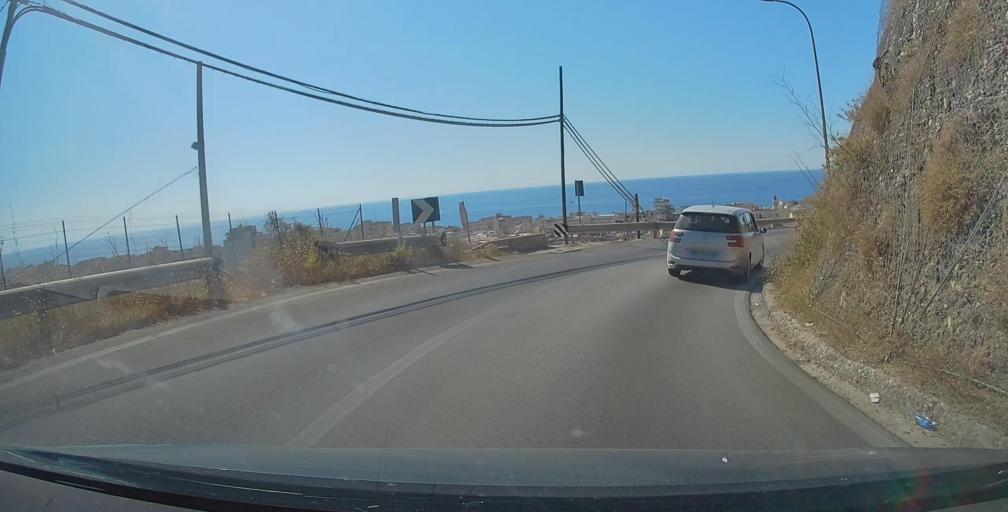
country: IT
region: Sicily
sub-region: Messina
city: Capo d'Orlando
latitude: 38.1584
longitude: 14.7488
